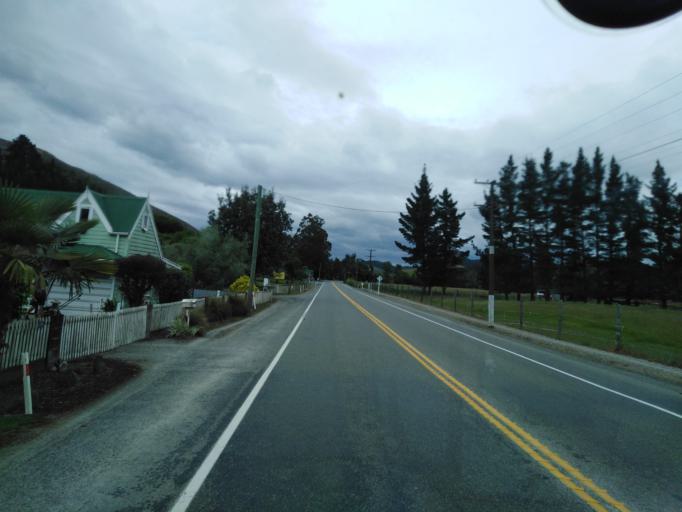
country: NZ
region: Tasman
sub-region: Tasman District
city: Wakefield
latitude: -41.4514
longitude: 172.9578
